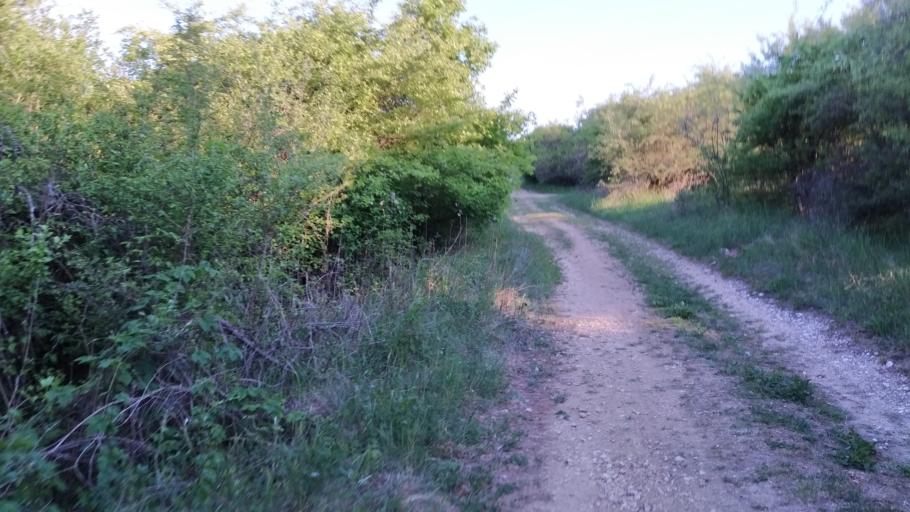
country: HU
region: Pest
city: Nagykovacsi
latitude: 47.6483
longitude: 18.9903
